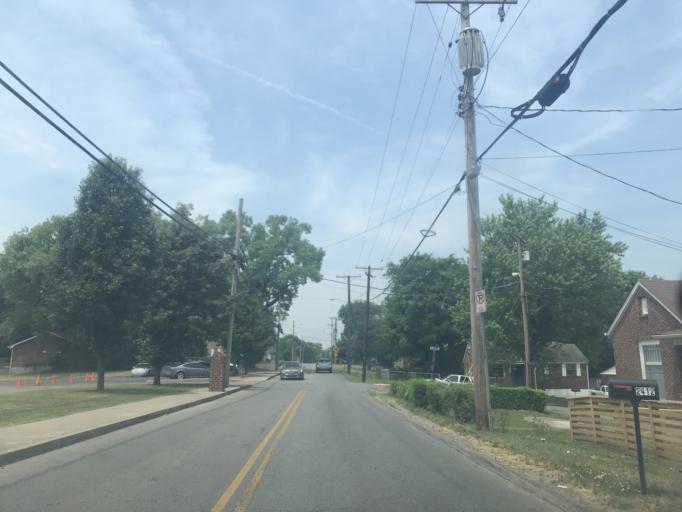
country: US
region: Tennessee
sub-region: Davidson County
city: Nashville
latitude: 36.1804
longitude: -86.8174
